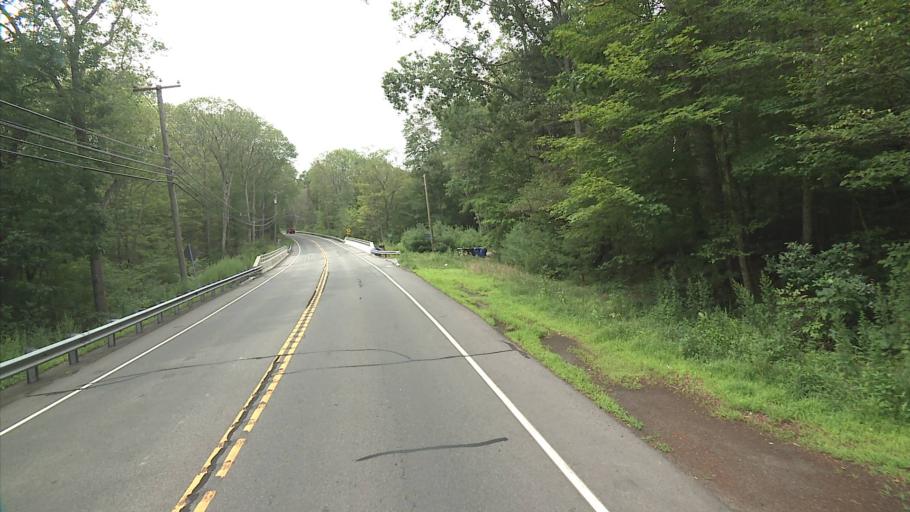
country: US
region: Connecticut
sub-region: Tolland County
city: Tolland
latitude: 41.8867
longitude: -72.3165
